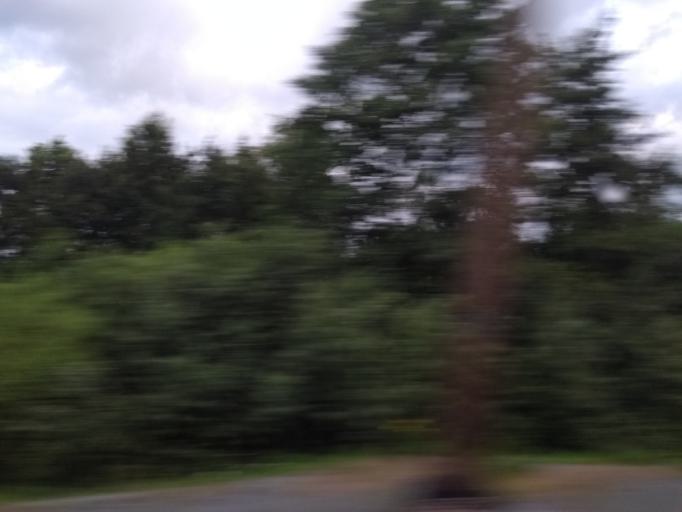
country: NL
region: Friesland
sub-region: Gemeente Heerenveen
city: Heerenveen
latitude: 52.9776
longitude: 5.8956
